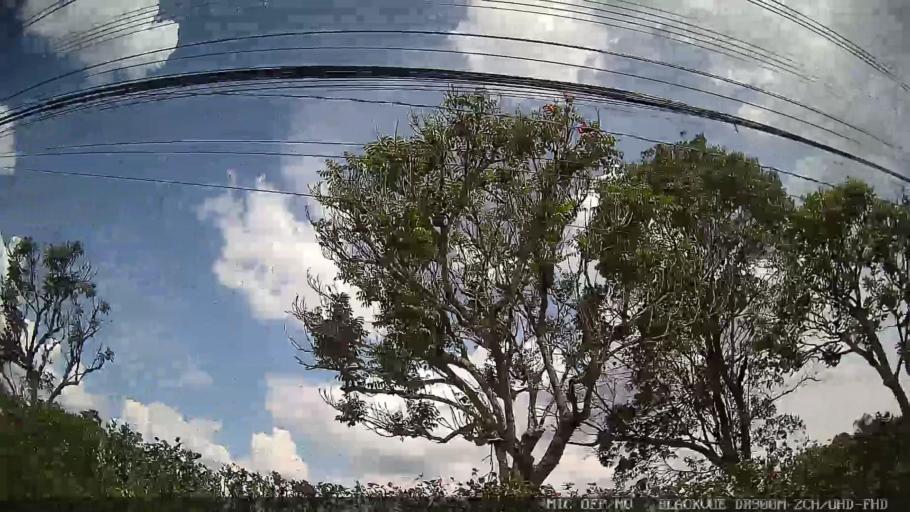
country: BR
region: Sao Paulo
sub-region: Braganca Paulista
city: Braganca Paulista
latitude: -22.9760
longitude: -46.5538
